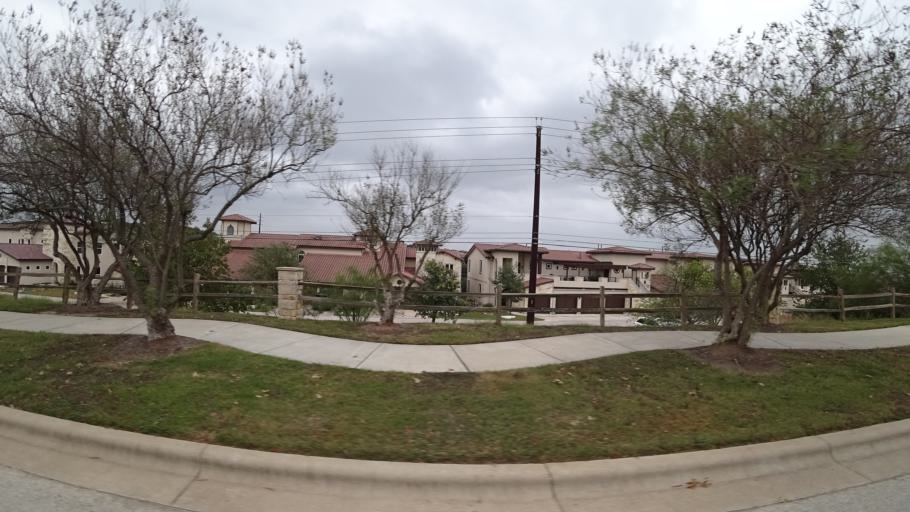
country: US
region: Texas
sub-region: Travis County
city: Hudson Bend
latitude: 30.3652
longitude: -97.8963
